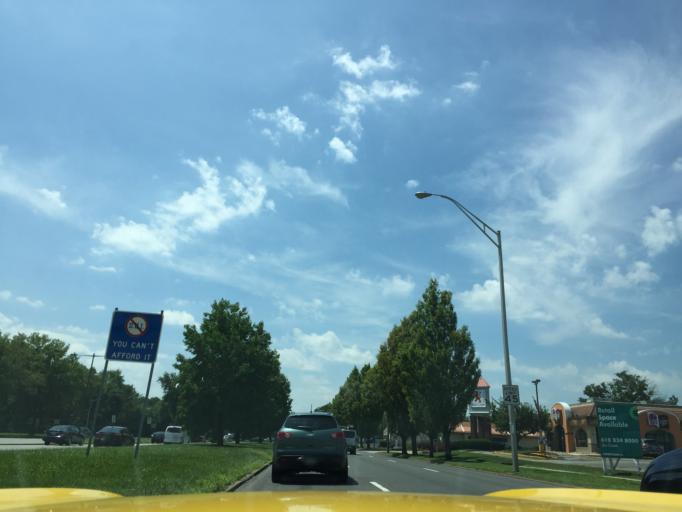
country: US
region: Pennsylvania
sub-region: Bucks County
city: Feasterville
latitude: 40.0946
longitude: -75.0158
